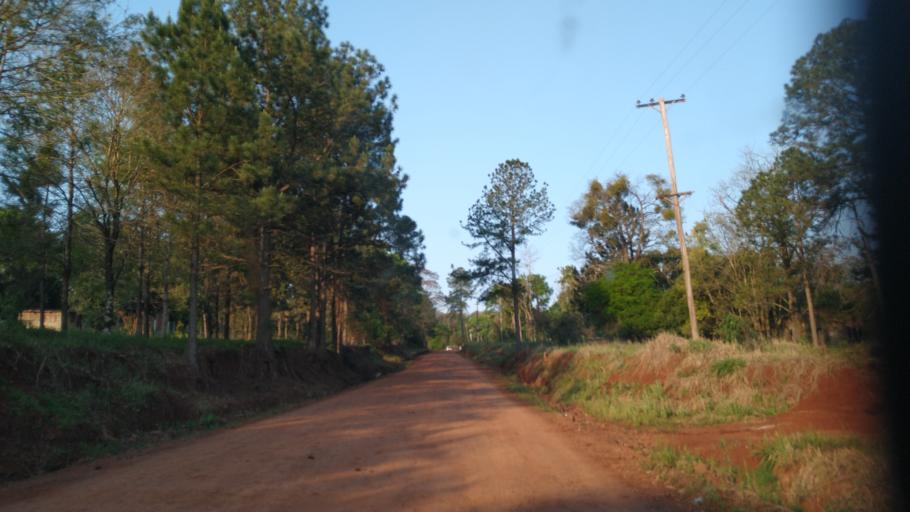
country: AR
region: Misiones
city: Jardin America
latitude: -27.0899
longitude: -55.2810
